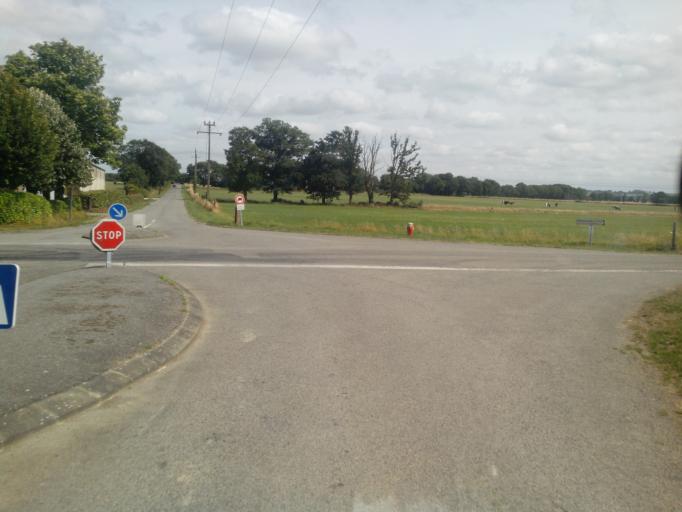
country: FR
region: Brittany
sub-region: Departement d'Ille-et-Vilaine
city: Messac
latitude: 47.8155
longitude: -1.8123
